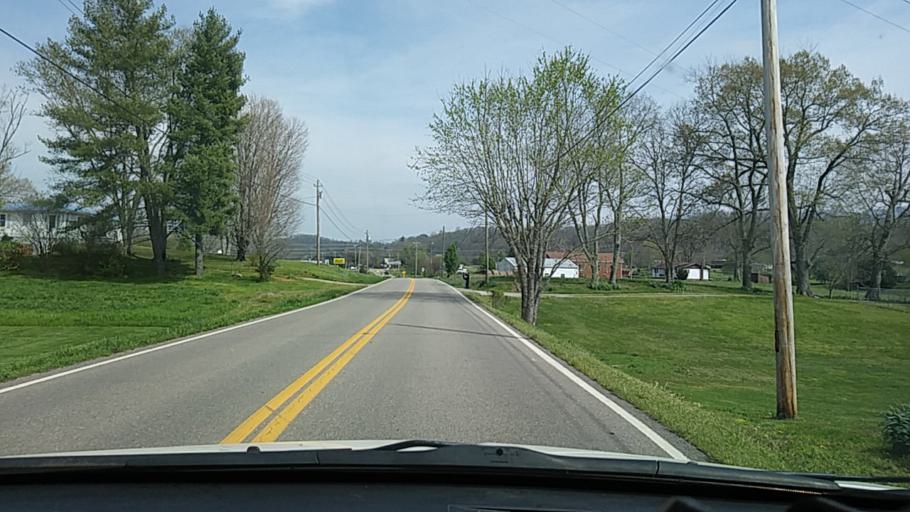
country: US
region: Tennessee
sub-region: Greene County
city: Tusculum
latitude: 36.1056
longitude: -82.7764
